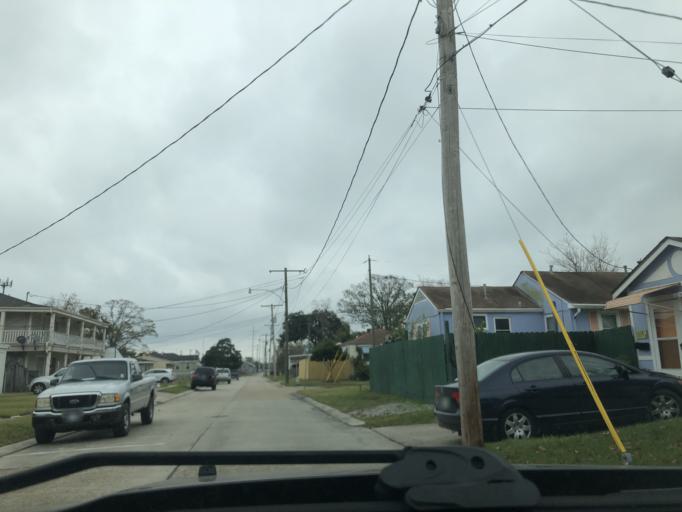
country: US
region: Louisiana
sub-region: Jefferson Parish
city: Metairie Terrace
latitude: 29.9725
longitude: -90.1657
